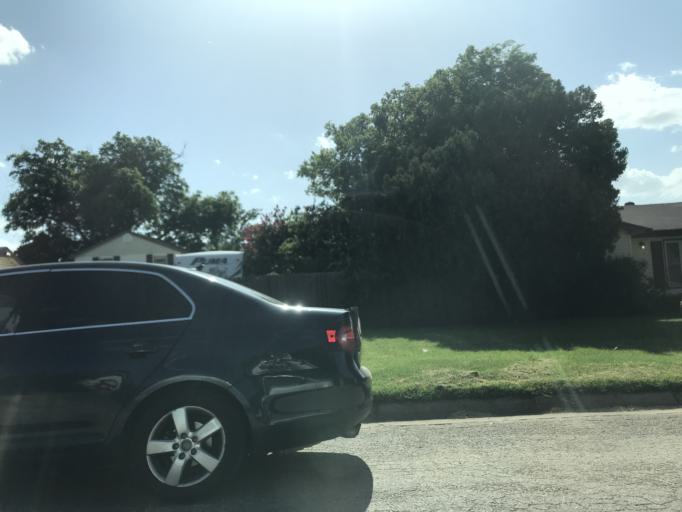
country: US
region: Texas
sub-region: Taylor County
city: Abilene
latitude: 32.4294
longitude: -99.7571
